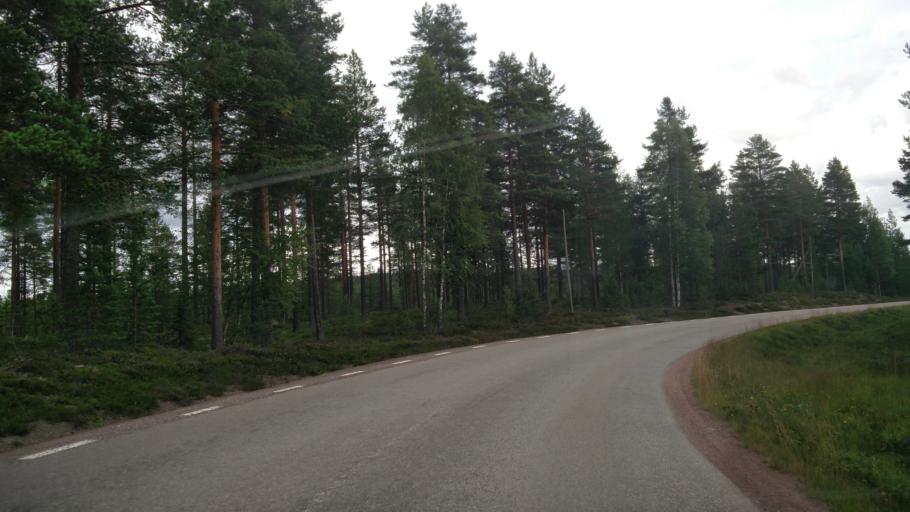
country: NO
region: Hedmark
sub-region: Trysil
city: Innbygda
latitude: 61.1713
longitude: 12.8414
